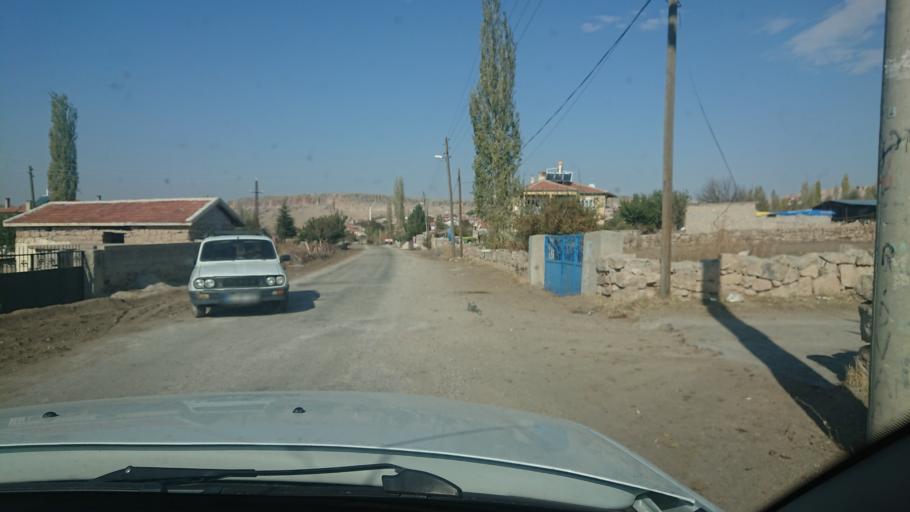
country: TR
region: Aksaray
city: Gulagac
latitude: 38.3501
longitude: 34.2351
